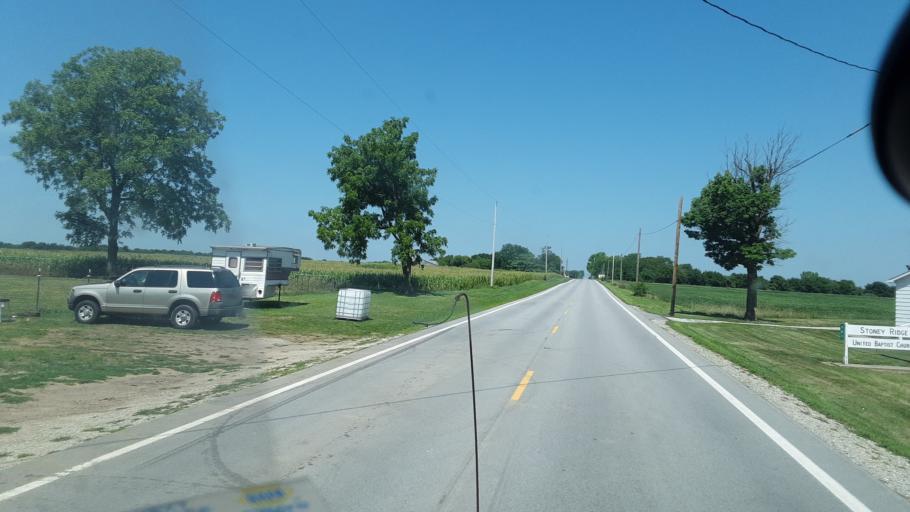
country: US
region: Ohio
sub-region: Wyandot County
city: Carey
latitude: 40.9777
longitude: -83.4406
